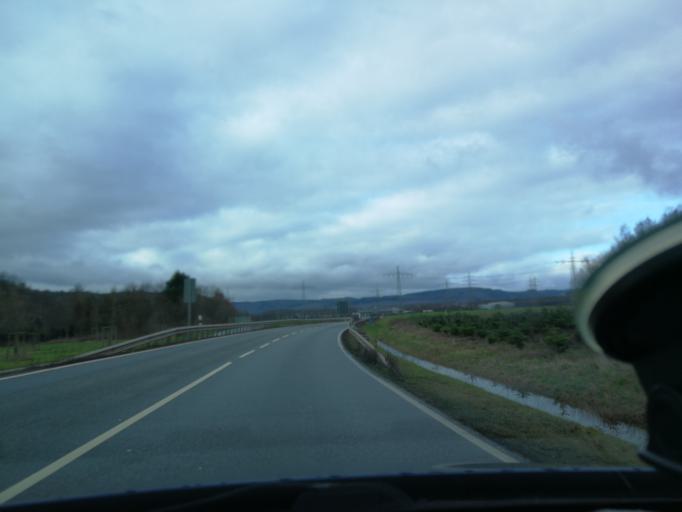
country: DE
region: Rheinland-Pfalz
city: Altrich
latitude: 49.9689
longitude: 6.9201
